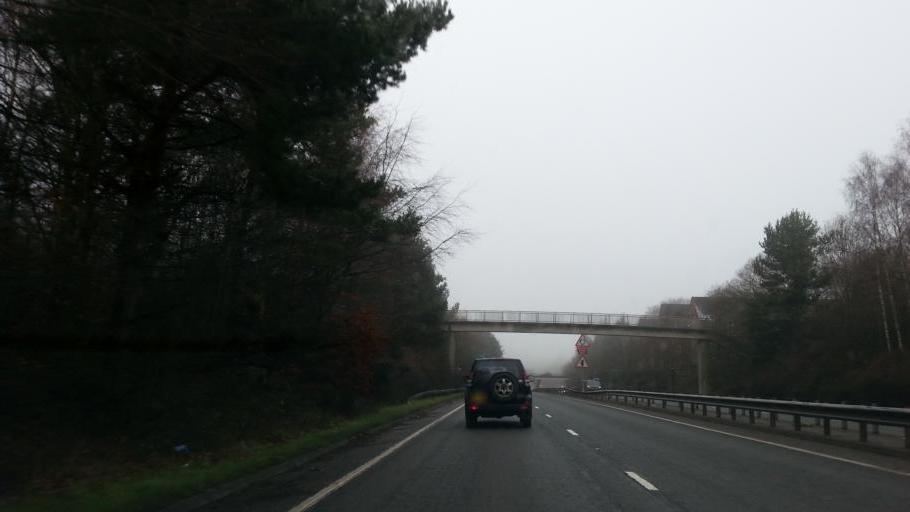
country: GB
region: England
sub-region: Cheshire East
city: Wilmslow
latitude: 53.3232
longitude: -2.2259
